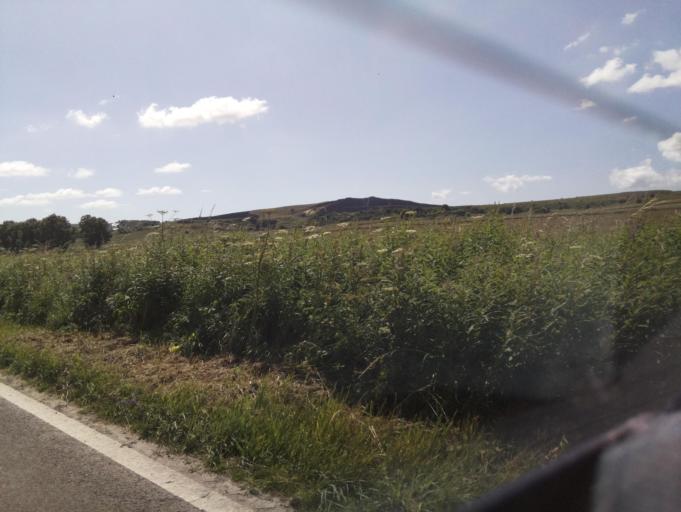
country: GB
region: England
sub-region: Derbyshire
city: Buxton
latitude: 53.2299
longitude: -1.8793
